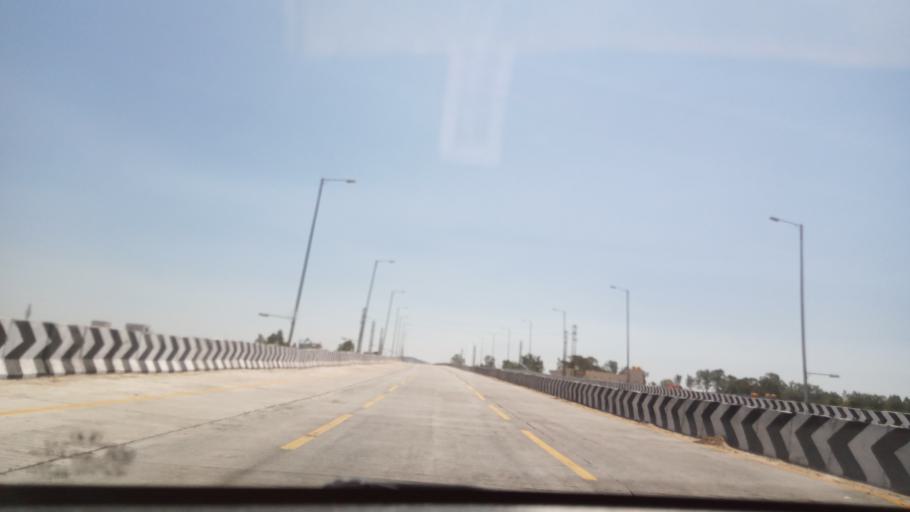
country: IN
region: Andhra Pradesh
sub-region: Chittoor
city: Palmaner
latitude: 13.1871
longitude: 78.6007
